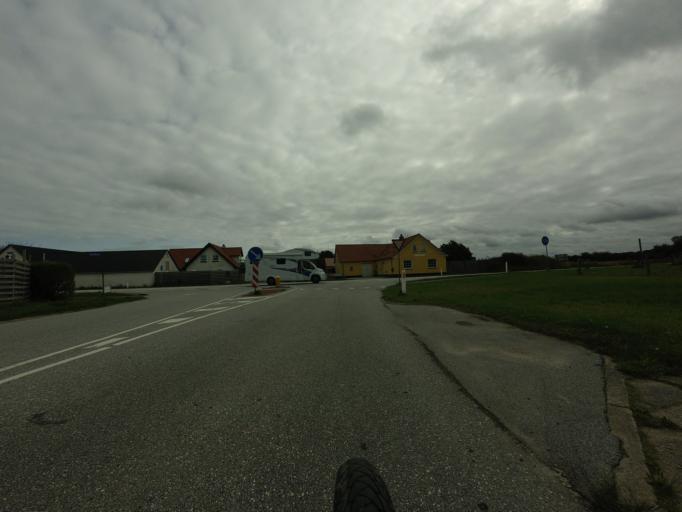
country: DK
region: North Denmark
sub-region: Hjorring Kommune
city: Hirtshals
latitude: 57.5550
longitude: 9.9383
